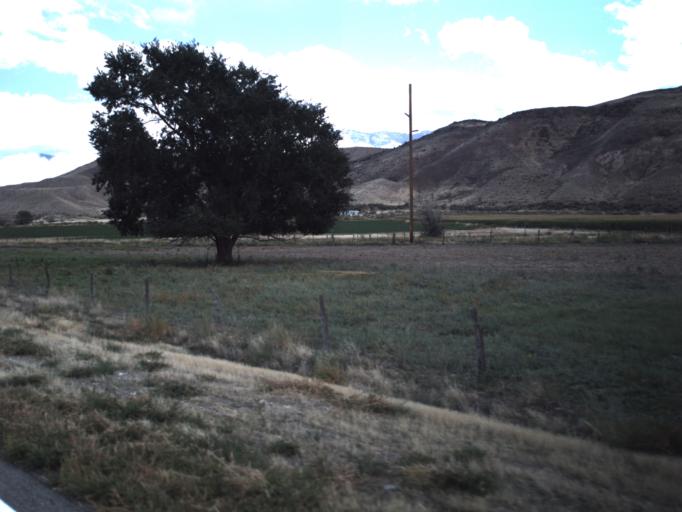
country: US
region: Utah
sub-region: Sevier County
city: Monroe
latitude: 38.6272
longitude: -112.2003
